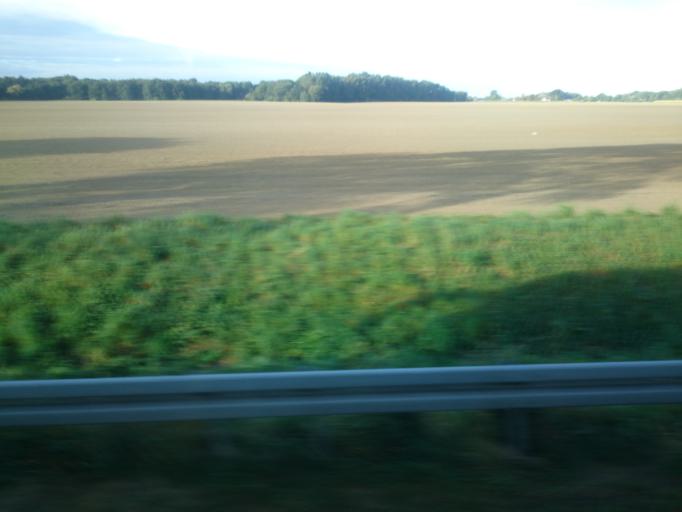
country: DE
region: Mecklenburg-Vorpommern
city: Anklam
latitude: 53.9024
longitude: 13.6644
